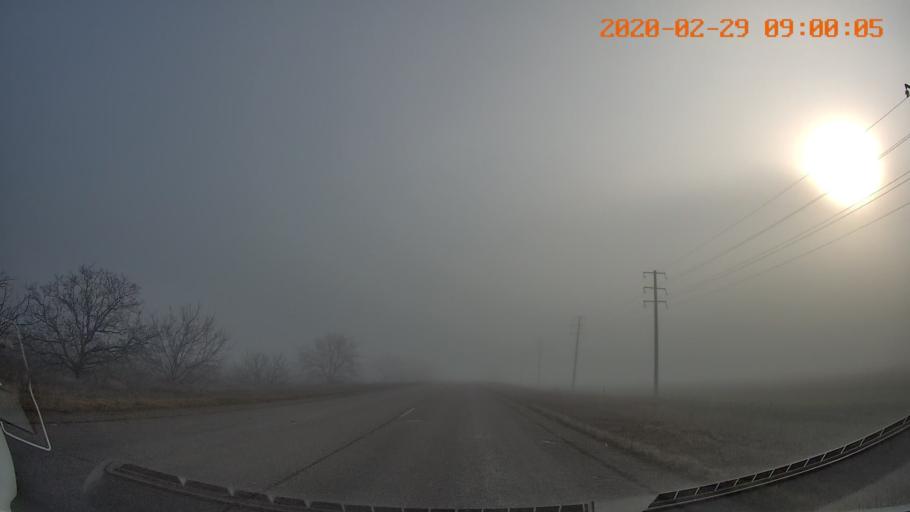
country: MD
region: Telenesti
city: Tiraspolul Nou
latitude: 46.9215
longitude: 29.6697
